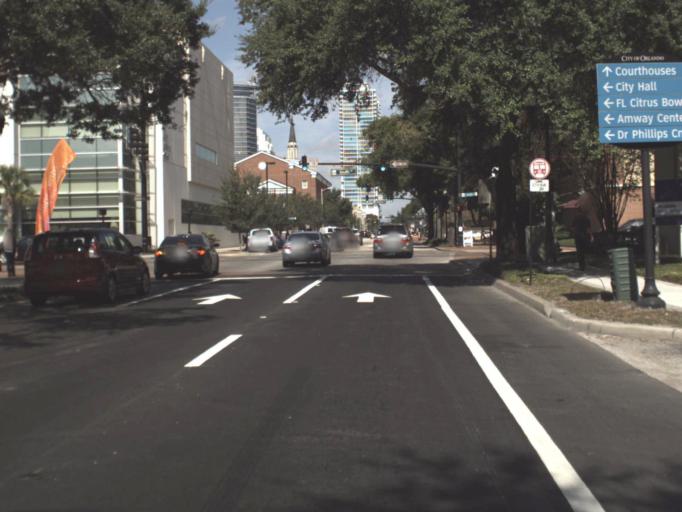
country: US
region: Florida
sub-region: Orange County
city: Orlando
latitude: 28.5379
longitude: -81.3758
